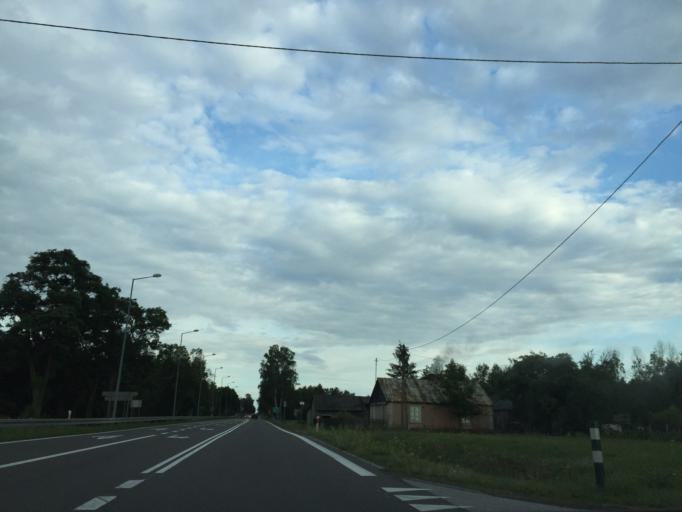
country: PL
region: Lublin Voivodeship
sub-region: Powiat lubartowski
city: Kock
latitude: 51.5990
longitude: 22.4735
